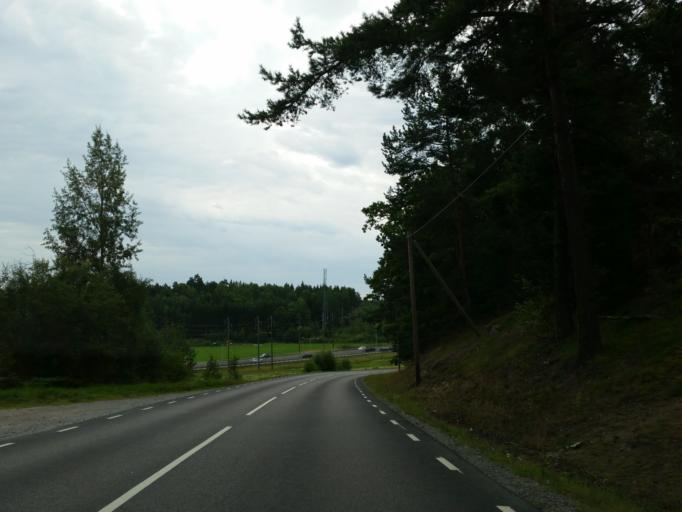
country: SE
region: Stockholm
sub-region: Botkyrka Kommun
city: Eriksberg
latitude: 59.2273
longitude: 17.7854
